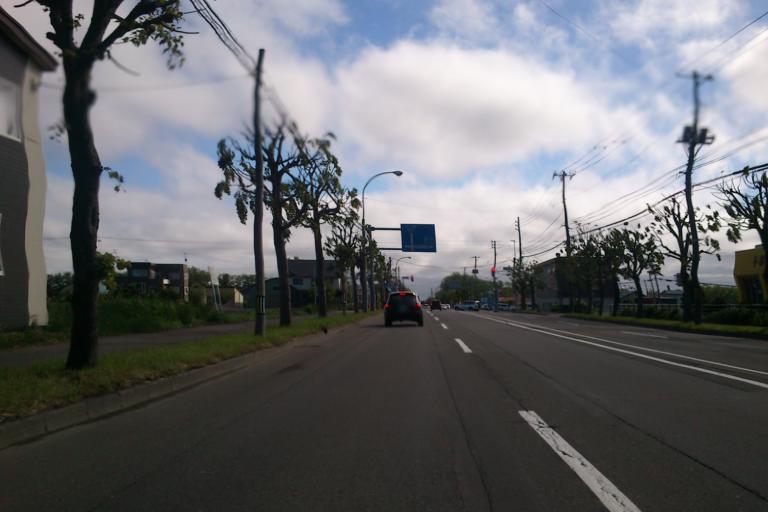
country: JP
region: Hokkaido
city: Sapporo
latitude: 43.1362
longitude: 141.2673
